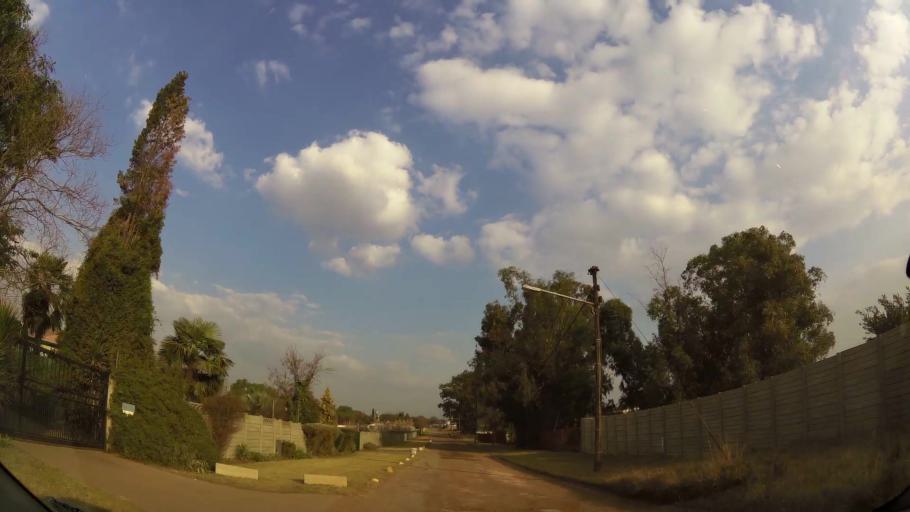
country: ZA
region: Gauteng
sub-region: Ekurhuleni Metropolitan Municipality
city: Benoni
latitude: -26.1223
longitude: 28.3055
